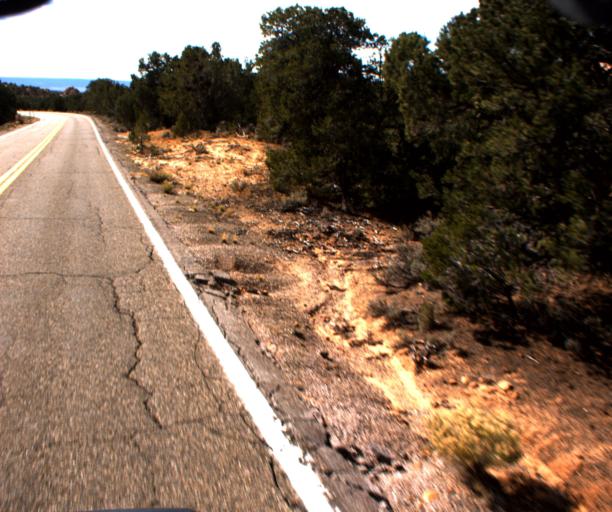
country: US
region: Arizona
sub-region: Navajo County
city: Kayenta
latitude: 36.6615
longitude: -110.5269
